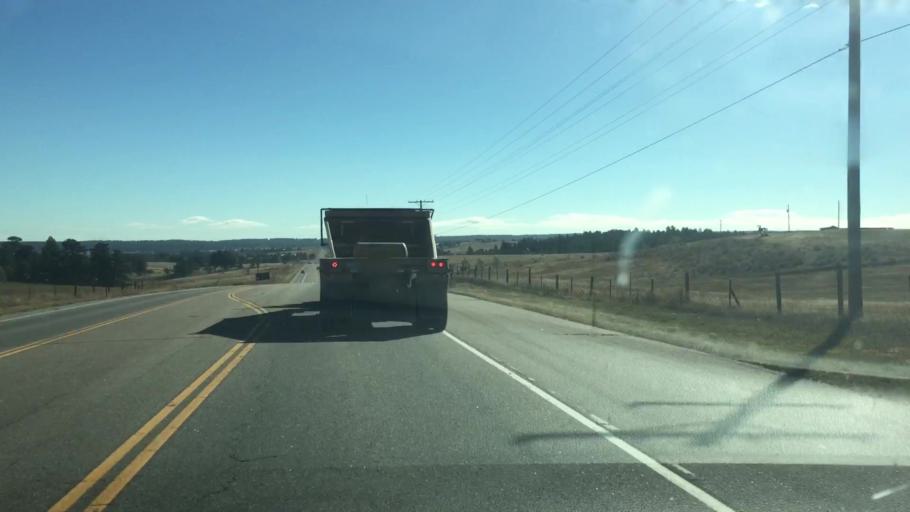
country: US
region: Colorado
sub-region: Elbert County
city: Ponderosa Park
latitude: 39.3620
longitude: -104.6573
